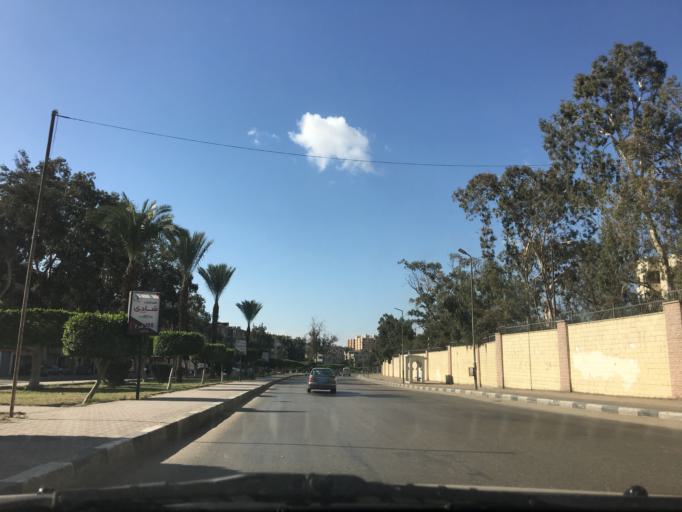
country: EG
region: Muhafazat al Qahirah
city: Cairo
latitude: 30.0508
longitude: 31.3200
